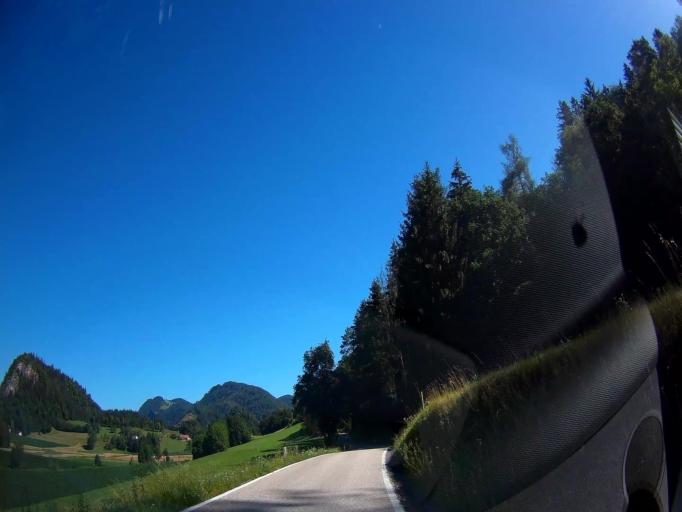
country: AT
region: Carinthia
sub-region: Politischer Bezirk Volkermarkt
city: Voelkermarkt
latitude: 46.6875
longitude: 14.5773
